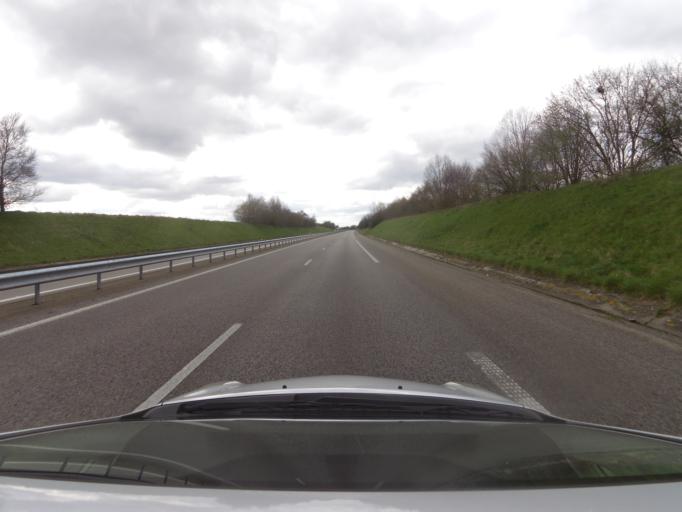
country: FR
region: Haute-Normandie
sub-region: Departement de la Seine-Maritime
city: Saint-Aubin-Routot
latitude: 49.5397
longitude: 0.3247
